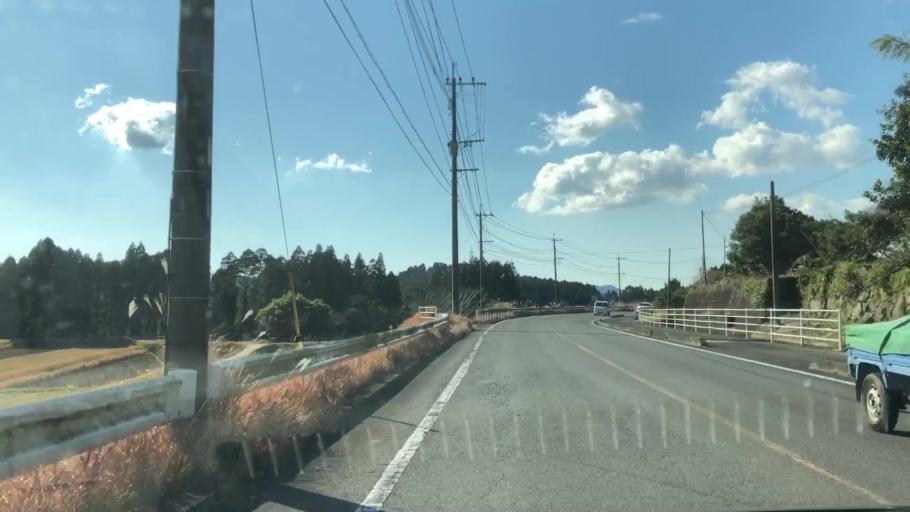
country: JP
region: Kagoshima
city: Satsumasendai
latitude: 31.8593
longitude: 130.4081
